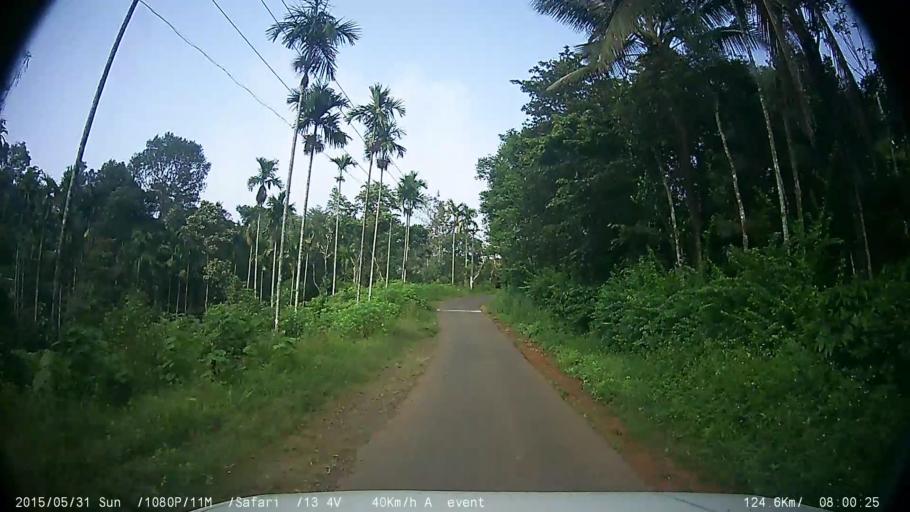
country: IN
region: Kerala
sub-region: Wayanad
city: Kalpetta
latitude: 11.6321
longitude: 76.0519
